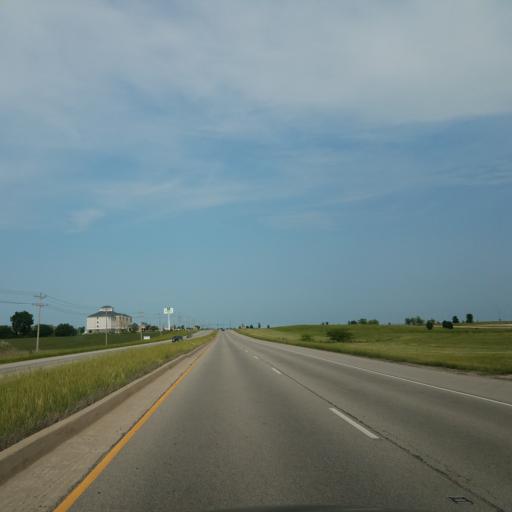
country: US
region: Illinois
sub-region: McLean County
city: Bloomington
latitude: 40.4882
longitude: -88.9173
